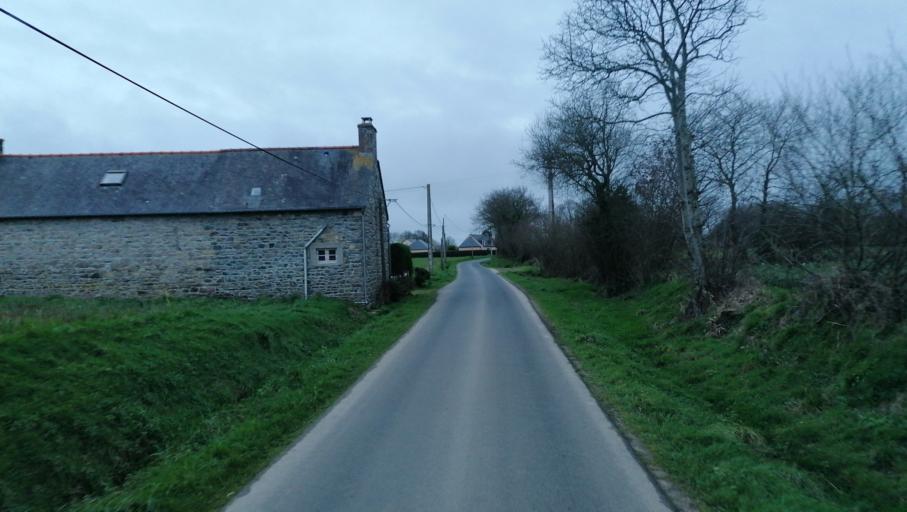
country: FR
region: Brittany
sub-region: Departement des Cotes-d'Armor
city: Saint-Agathon
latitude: 48.5712
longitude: -3.0575
